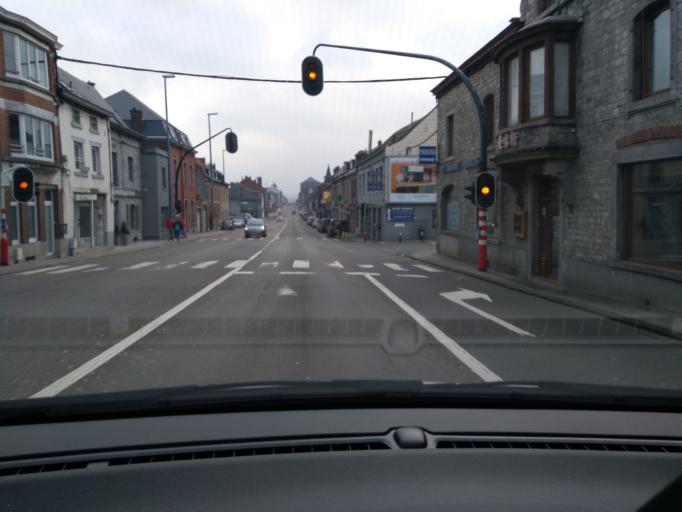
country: BE
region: Wallonia
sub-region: Province de Namur
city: Namur
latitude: 50.4722
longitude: 4.8258
